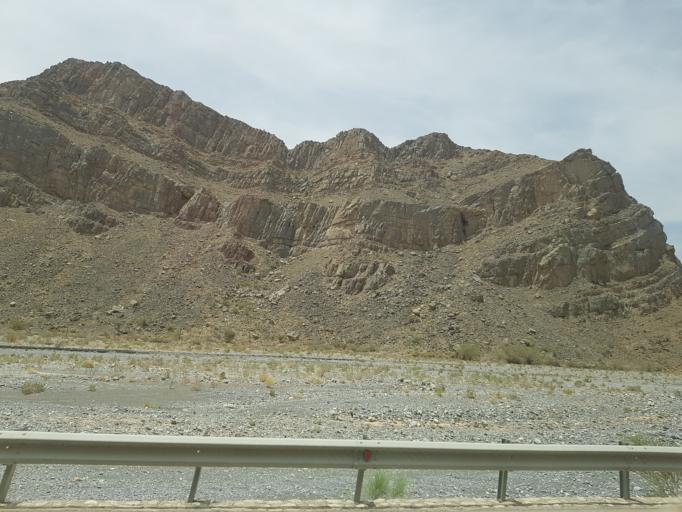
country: OM
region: Muhafazat ad Dakhiliyah
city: Izki
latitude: 22.9425
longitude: 57.6735
